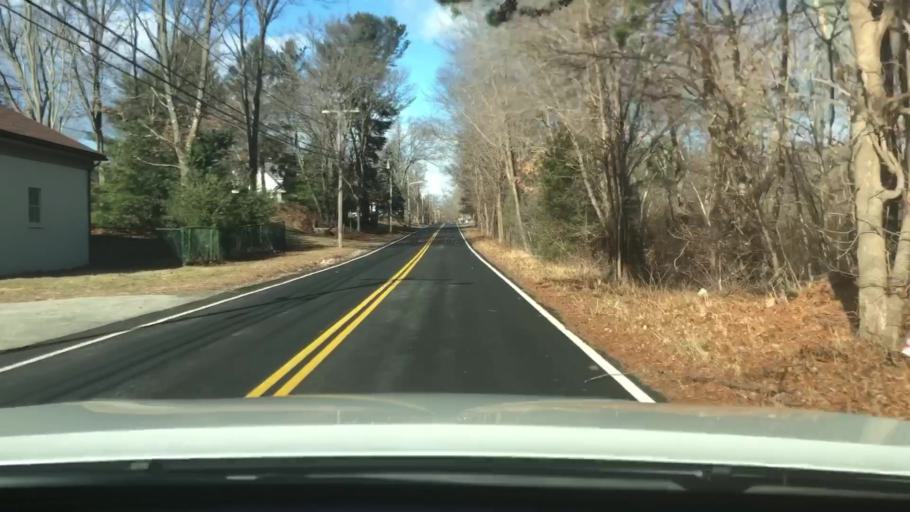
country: US
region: Rhode Island
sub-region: Providence County
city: Woonsocket
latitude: 42.0298
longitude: -71.5148
